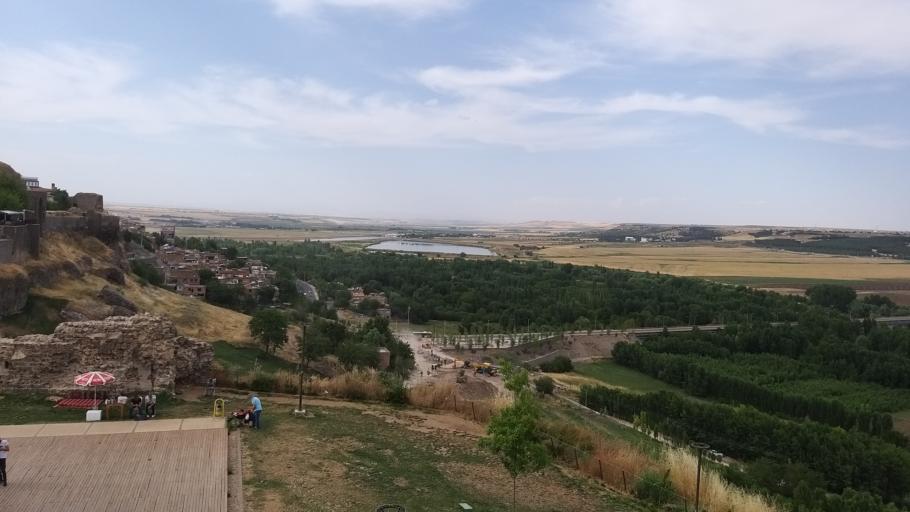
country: TR
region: Diyarbakir
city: Sur
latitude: 37.9144
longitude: 40.2438
